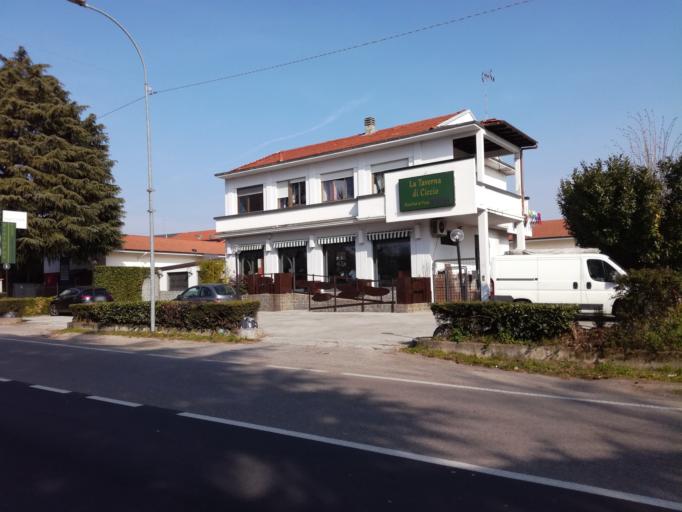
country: IT
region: Lombardy
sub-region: Provincia di Monza e Brianza
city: Lentate sul Seveso
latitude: 45.6873
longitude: 9.1098
